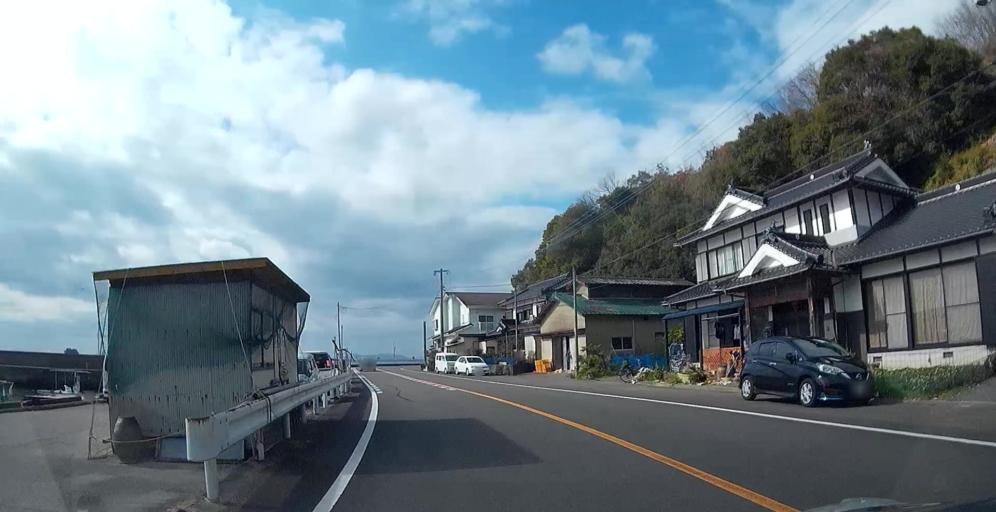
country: JP
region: Kumamoto
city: Minamata
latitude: 32.3119
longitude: 130.4705
